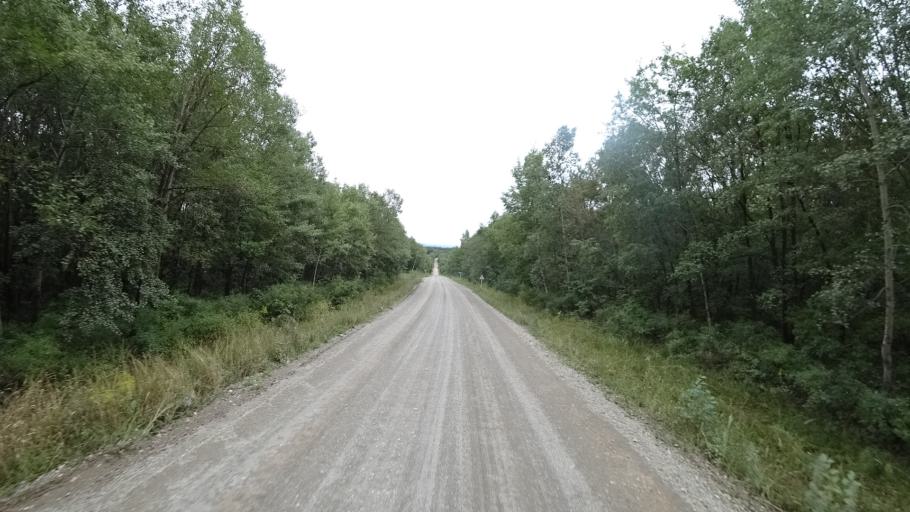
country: RU
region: Primorskiy
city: Ivanovka
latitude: 44.0320
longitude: 132.5060
